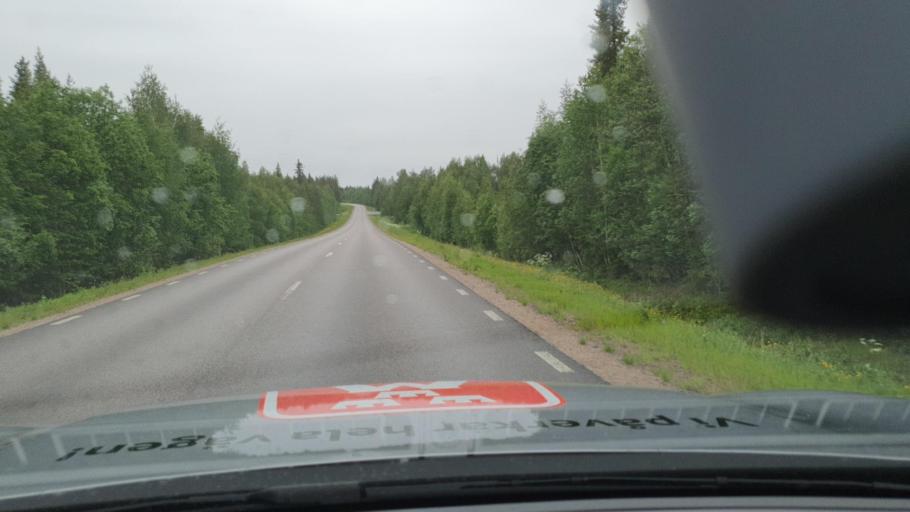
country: SE
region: Norrbotten
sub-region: Overtornea Kommun
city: OEvertornea
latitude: 66.4041
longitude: 23.4824
